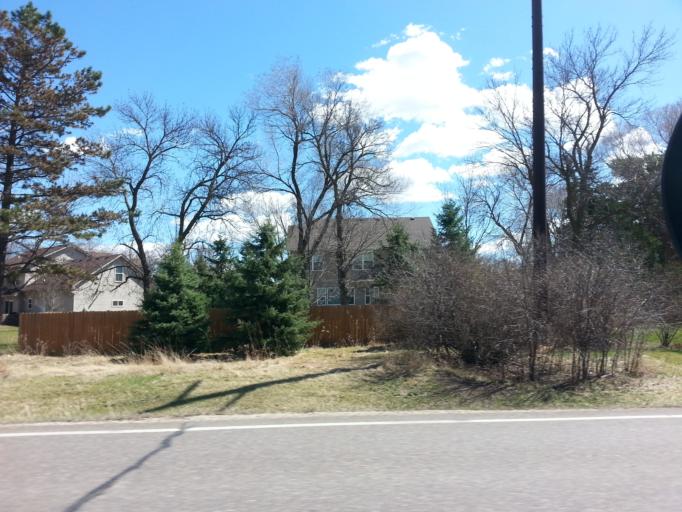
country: US
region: Minnesota
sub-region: Dakota County
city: Apple Valley
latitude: 44.7090
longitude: -93.1937
